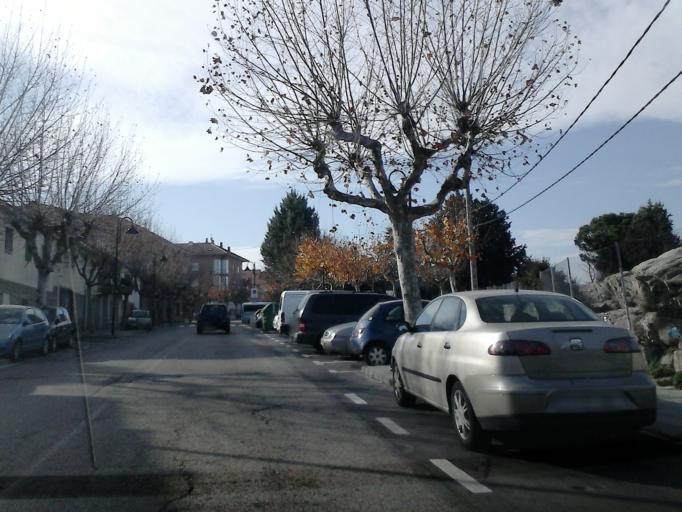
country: ES
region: Madrid
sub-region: Provincia de Madrid
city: Galapagar
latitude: 40.5815
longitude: -4.0011
